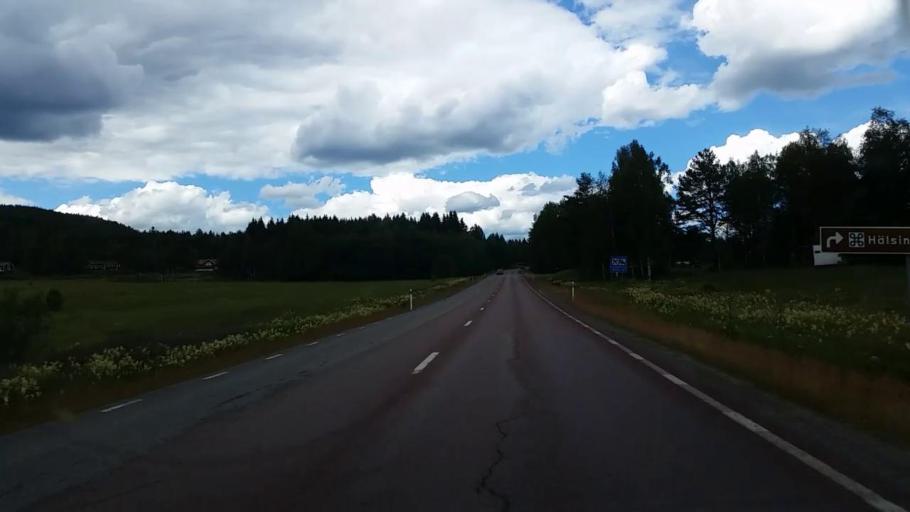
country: SE
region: Gaevleborg
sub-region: Ljusdals Kommun
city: Jaervsoe
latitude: 61.6802
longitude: 16.1455
